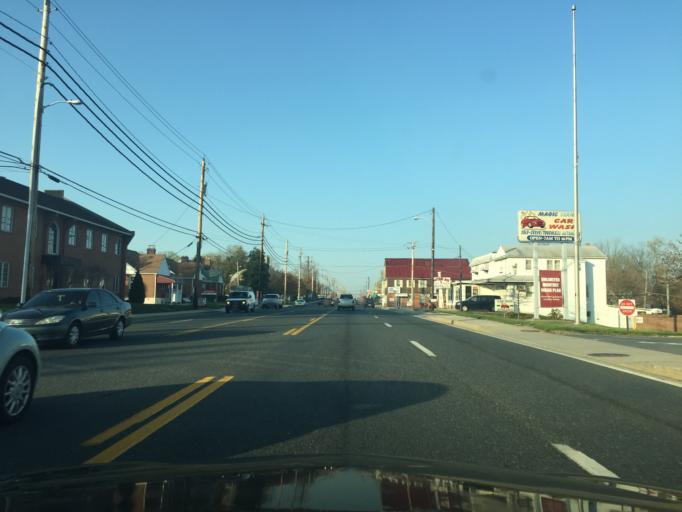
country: US
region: Maryland
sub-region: Baltimore County
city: Perry Hall
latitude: 39.4095
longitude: -76.4676
